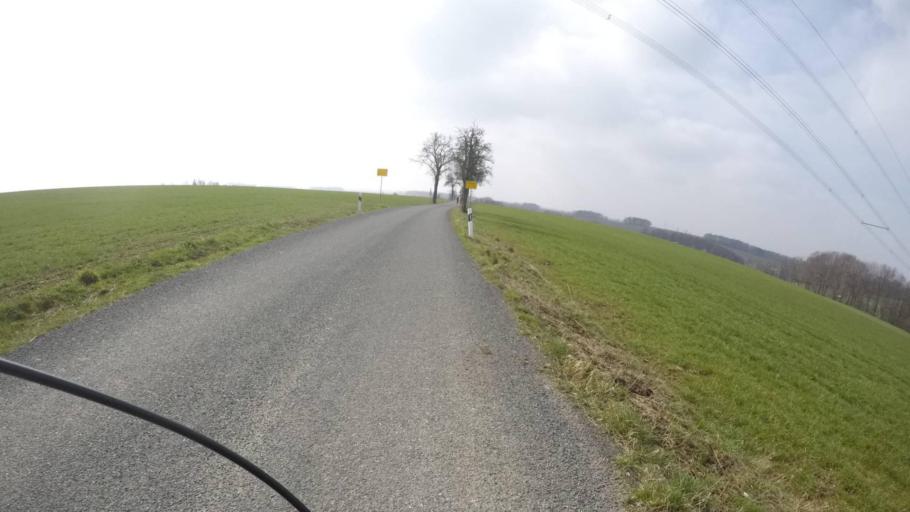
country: DE
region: Saxony
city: Niederfrohna
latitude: 50.8778
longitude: 12.6959
